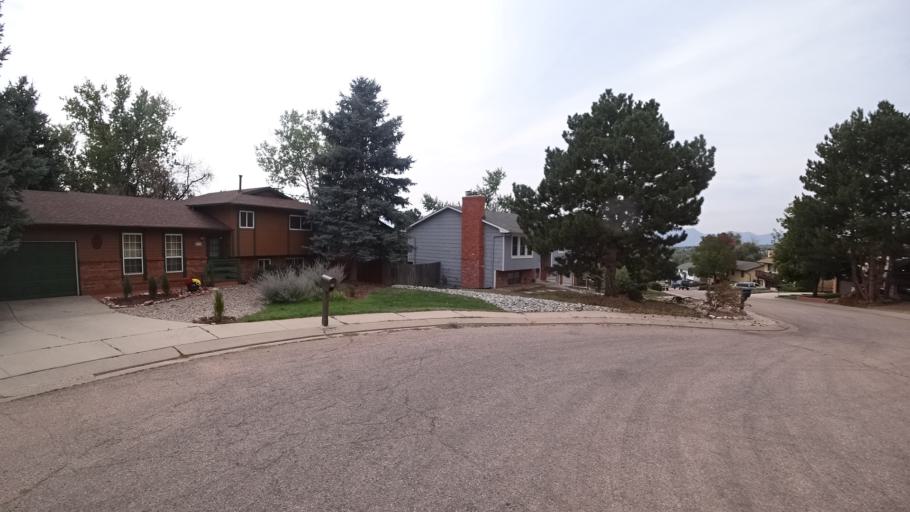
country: US
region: Colorado
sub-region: El Paso County
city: Cimarron Hills
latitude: 38.9000
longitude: -104.7307
